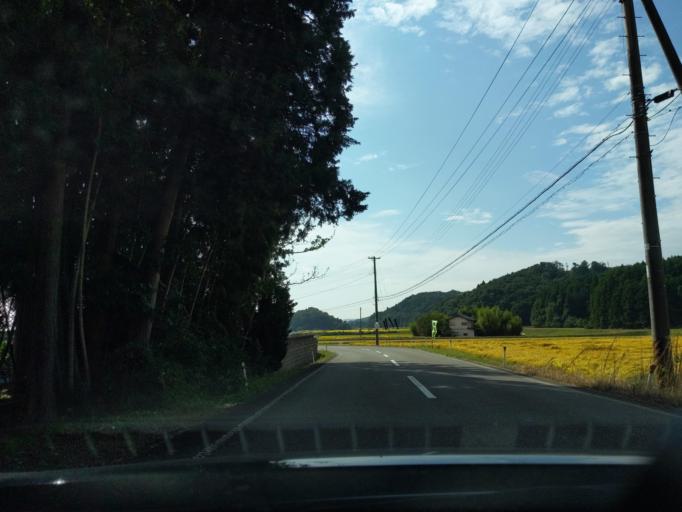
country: JP
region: Fukushima
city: Koriyama
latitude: 37.3852
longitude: 140.2605
